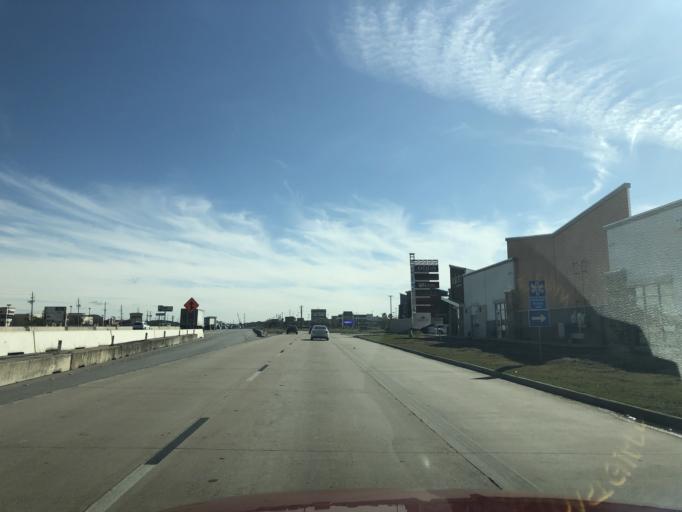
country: US
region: Texas
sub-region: Galveston County
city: League City
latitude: 29.4734
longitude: -95.0968
